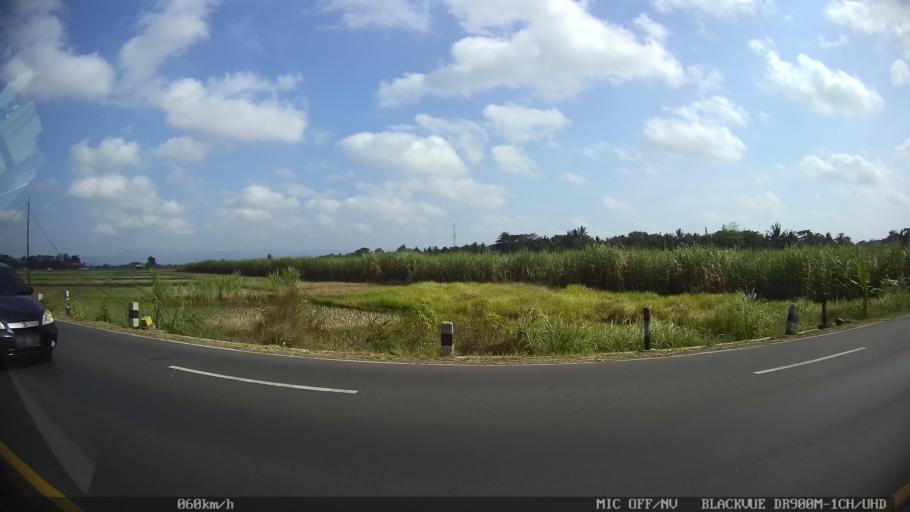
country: ID
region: Daerah Istimewa Yogyakarta
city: Godean
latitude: -7.8183
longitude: 110.2452
